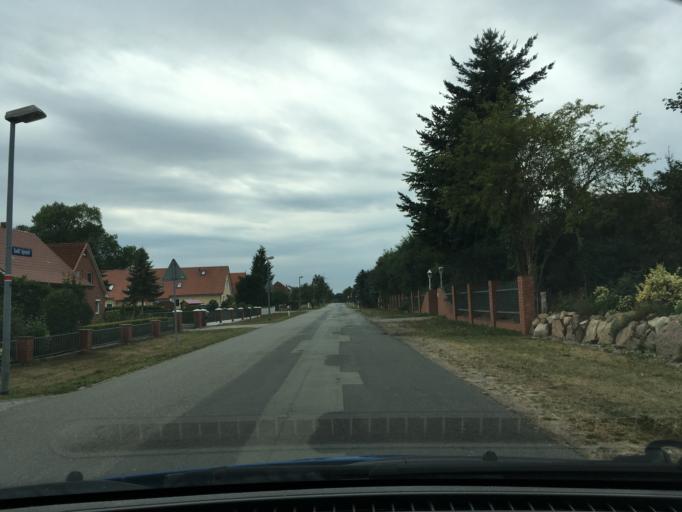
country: DE
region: Mecklenburg-Vorpommern
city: Wittenburg
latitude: 53.5164
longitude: 11.1188
